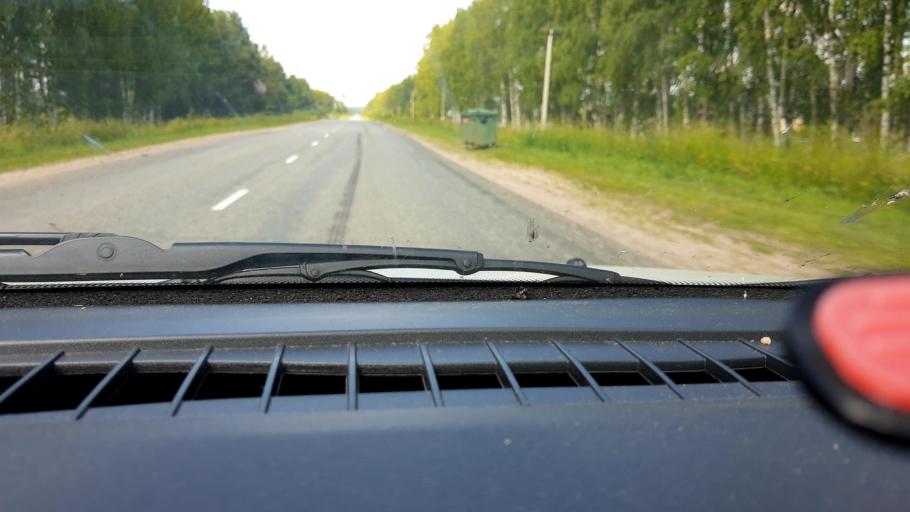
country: RU
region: Nizjnij Novgorod
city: Tonkino
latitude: 57.2744
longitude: 46.4612
